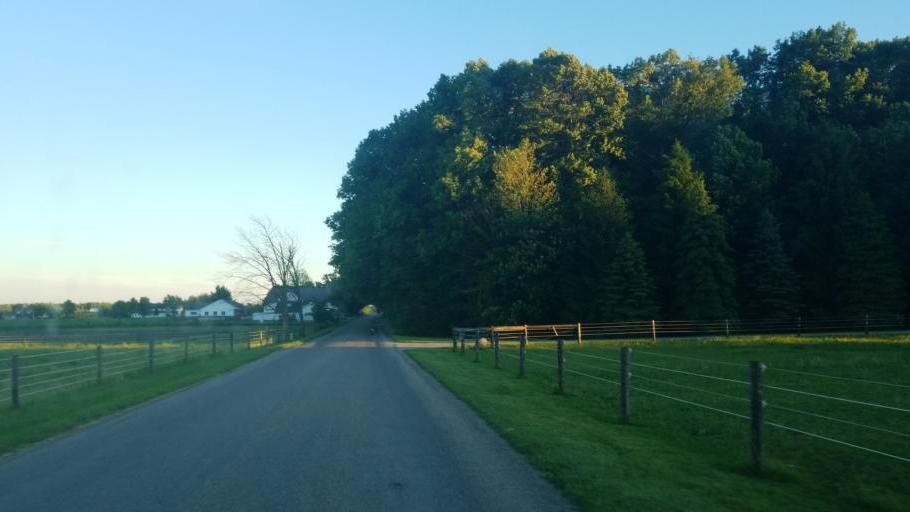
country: US
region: Indiana
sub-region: Elkhart County
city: Nappanee
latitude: 41.4303
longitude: -86.0300
